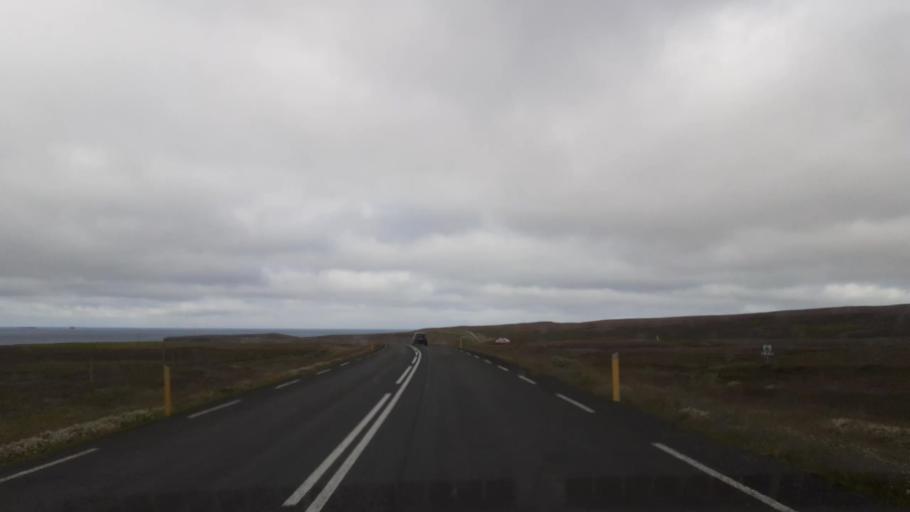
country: IS
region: Northeast
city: Husavik
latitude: 66.1771
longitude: -17.1726
